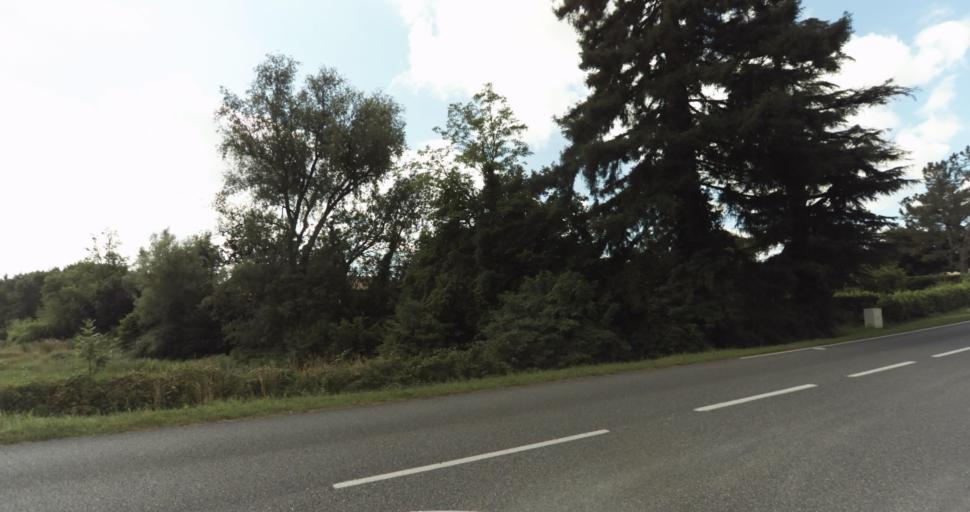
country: FR
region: Aquitaine
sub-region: Departement de la Gironde
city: Bazas
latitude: 44.4376
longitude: -0.2052
